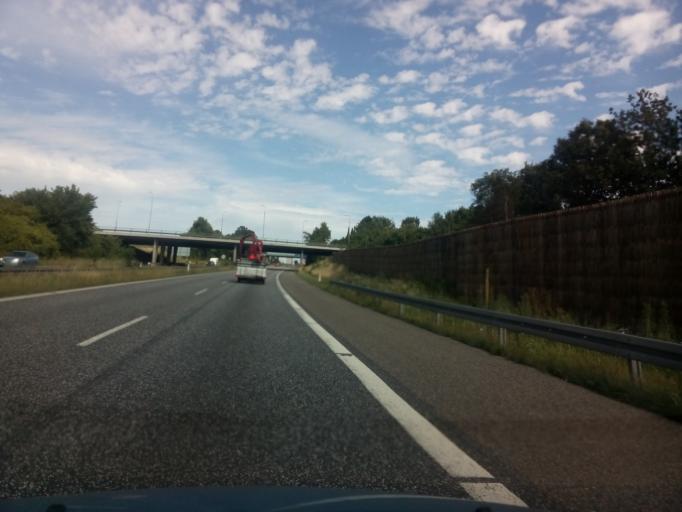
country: DK
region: Central Jutland
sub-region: Randers Kommune
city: Randers
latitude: 56.4608
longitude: 9.9875
